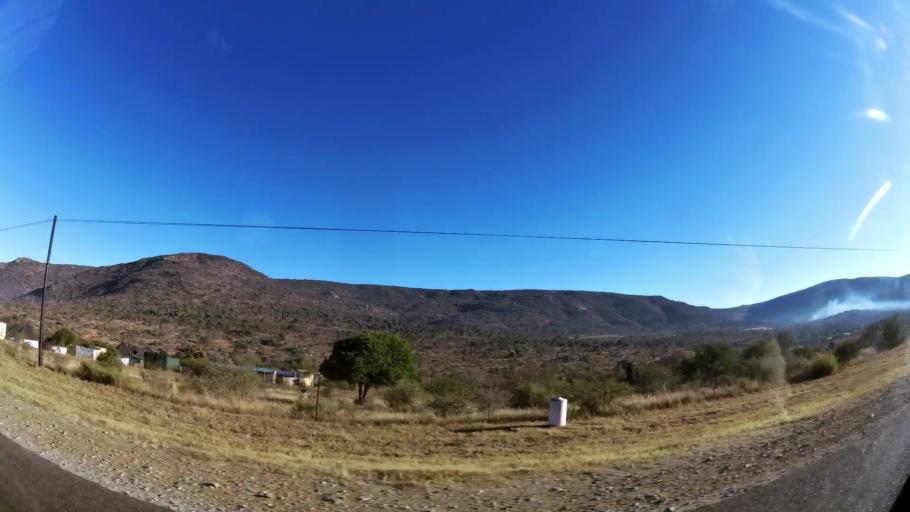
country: ZA
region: Limpopo
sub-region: Capricorn District Municipality
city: Mankoeng
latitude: -23.9390
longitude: 29.8281
